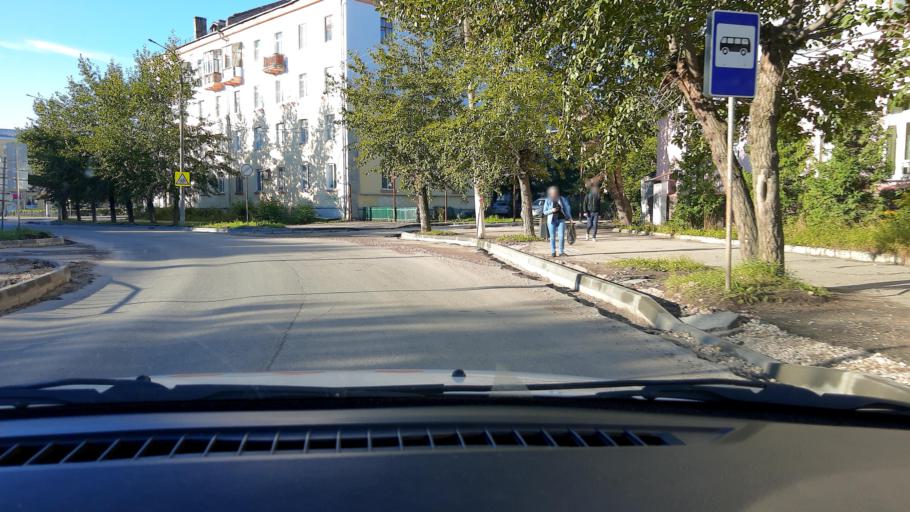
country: RU
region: Nizjnij Novgorod
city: Dzerzhinsk
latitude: 56.2440
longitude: 43.4714
